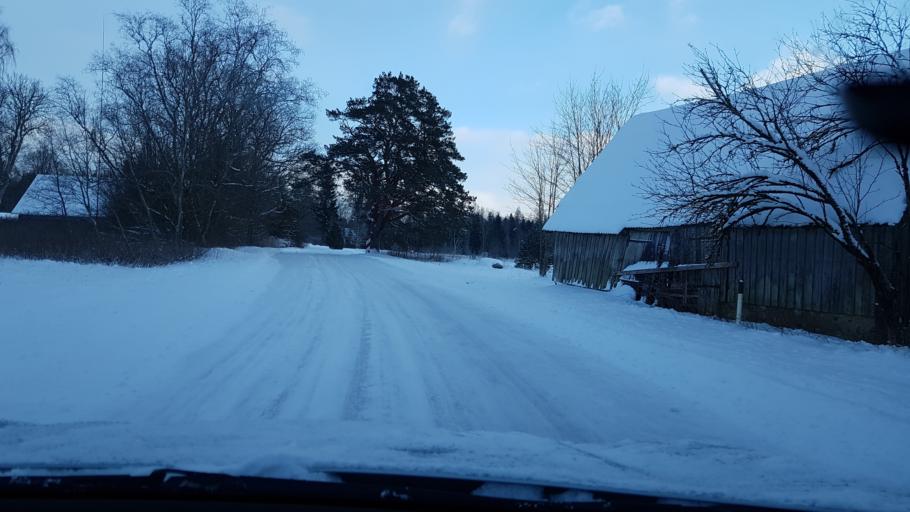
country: EE
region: Harju
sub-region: Nissi vald
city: Turba
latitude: 59.1526
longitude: 24.1462
